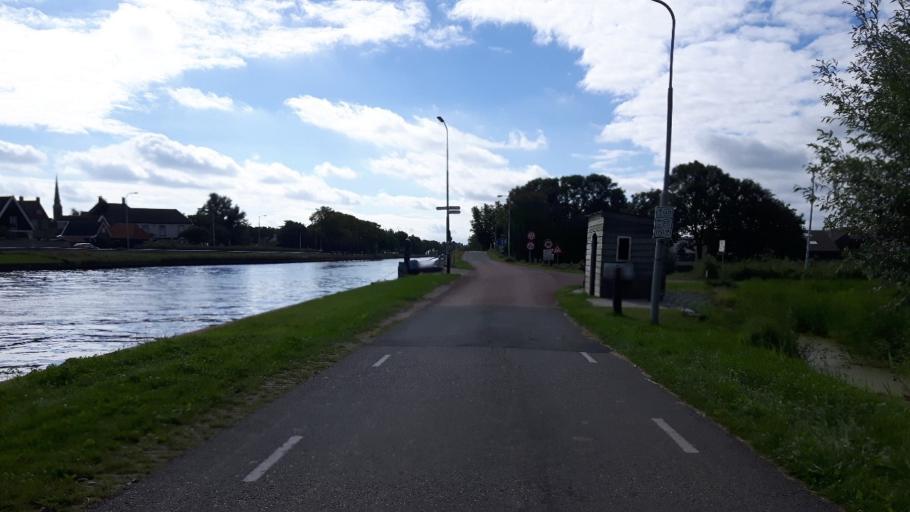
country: NL
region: North Holland
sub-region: Gemeente Purmerend
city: Purmerend
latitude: 52.4639
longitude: 4.9485
